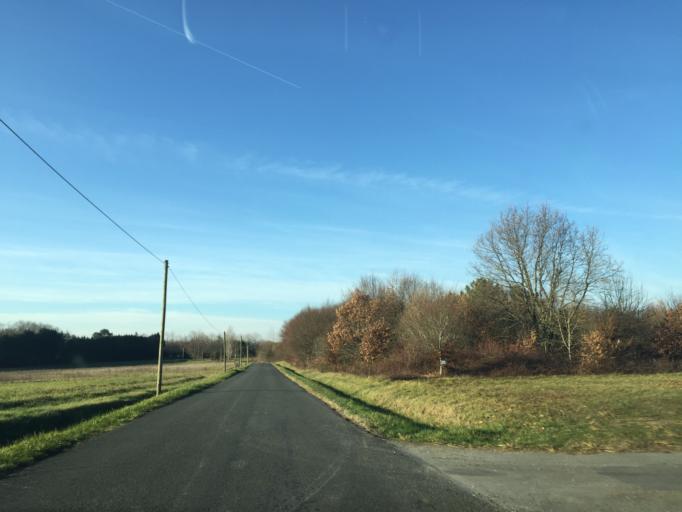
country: FR
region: Aquitaine
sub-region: Departement de la Dordogne
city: Riberac
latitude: 45.2035
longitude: 0.3176
